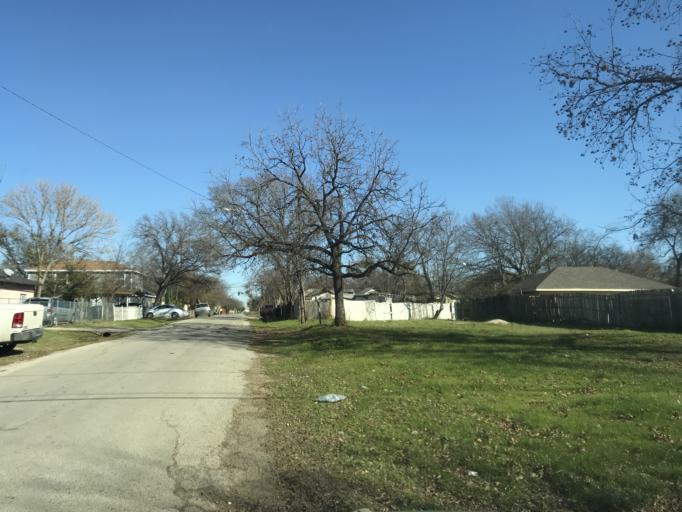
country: US
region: Texas
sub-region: Dallas County
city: Cockrell Hill
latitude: 32.7711
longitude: -96.9093
